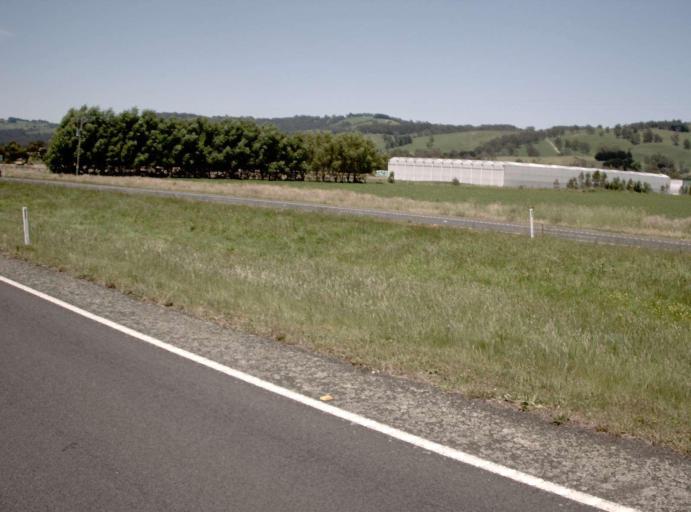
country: AU
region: Victoria
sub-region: Baw Baw
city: Warragul
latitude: -38.2059
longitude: 146.0933
